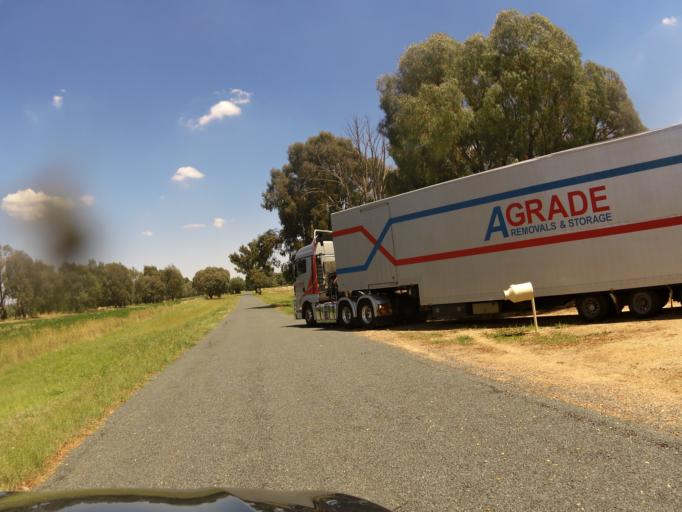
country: AU
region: Victoria
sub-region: Wangaratta
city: Wangaratta
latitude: -36.4293
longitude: 146.5505
